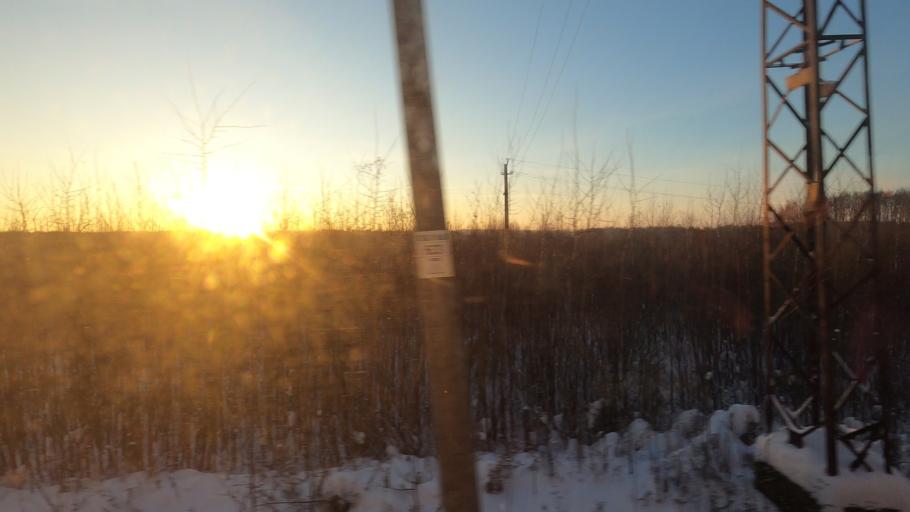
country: RU
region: Moskovskaya
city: Dmitrov
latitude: 56.3769
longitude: 37.5212
